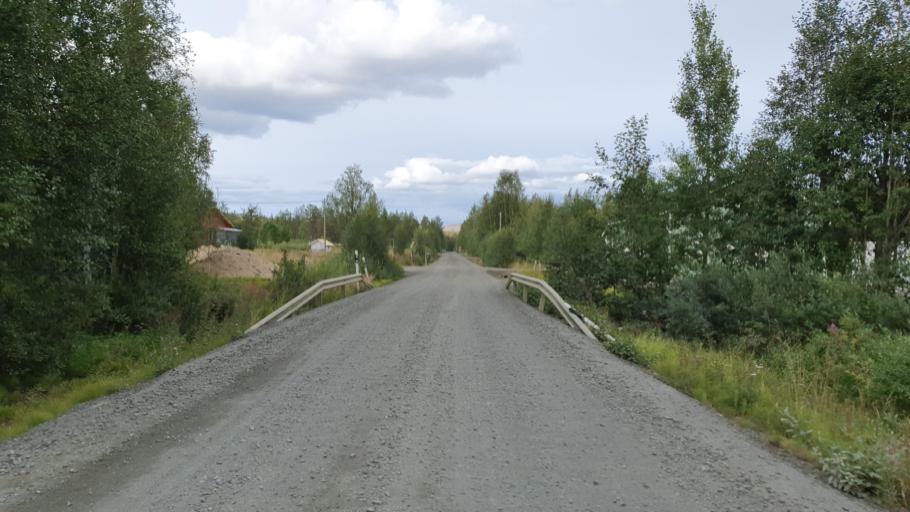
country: FI
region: Lapland
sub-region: Tunturi-Lappi
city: Kolari
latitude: 67.6225
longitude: 24.1616
